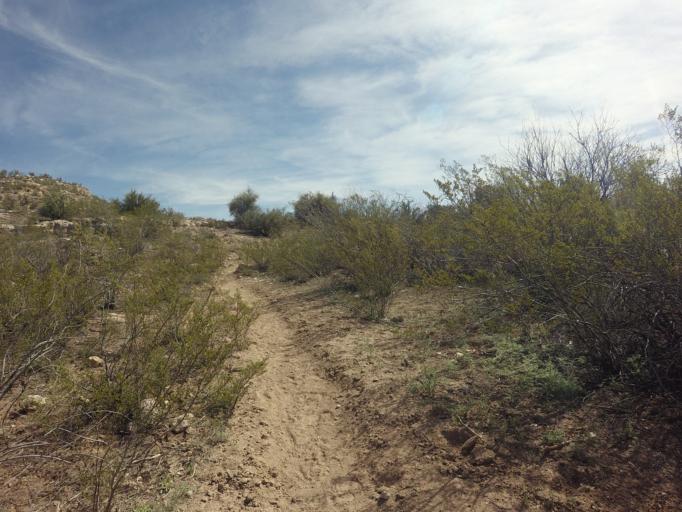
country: US
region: Arizona
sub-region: Yavapai County
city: Cottonwood
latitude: 34.7550
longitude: -112.0147
